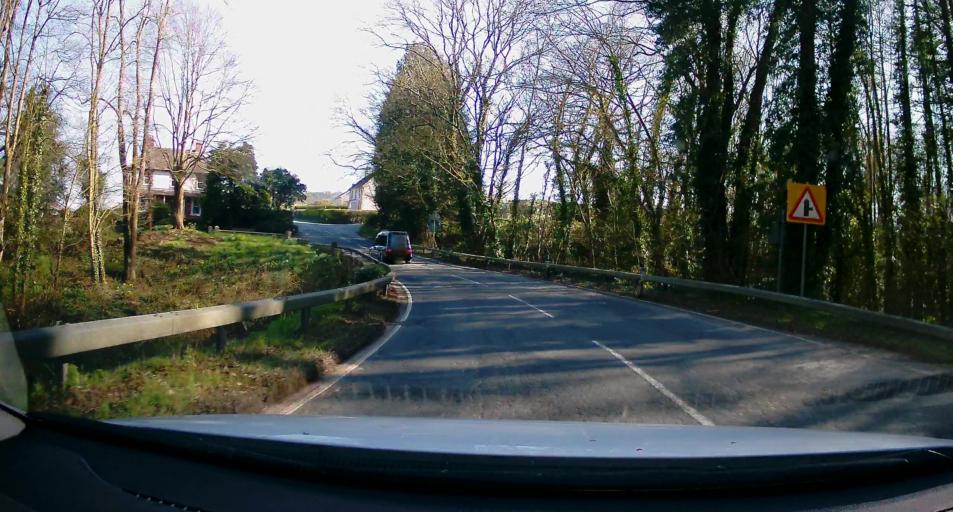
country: GB
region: Wales
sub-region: County of Ceredigion
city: Penparcau
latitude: 52.3624
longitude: -4.0582
